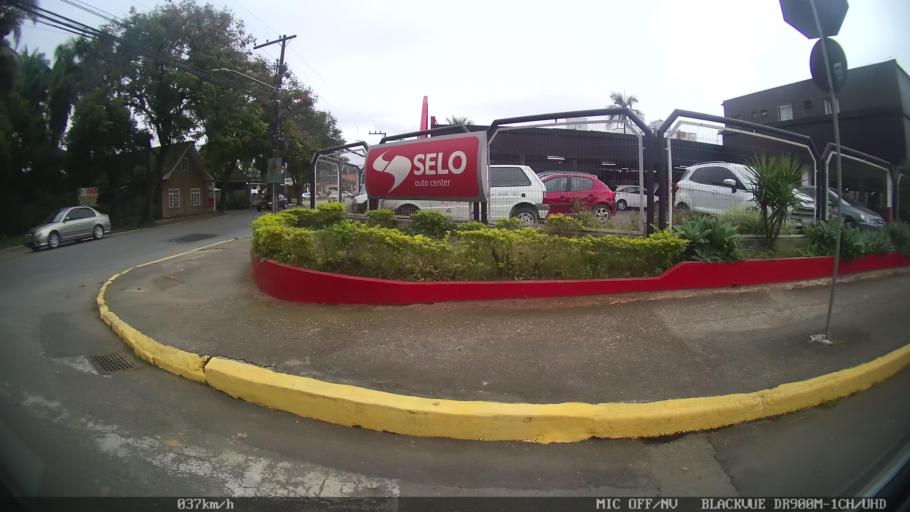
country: BR
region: Santa Catarina
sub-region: Joinville
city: Joinville
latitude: -26.2850
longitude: -48.8401
